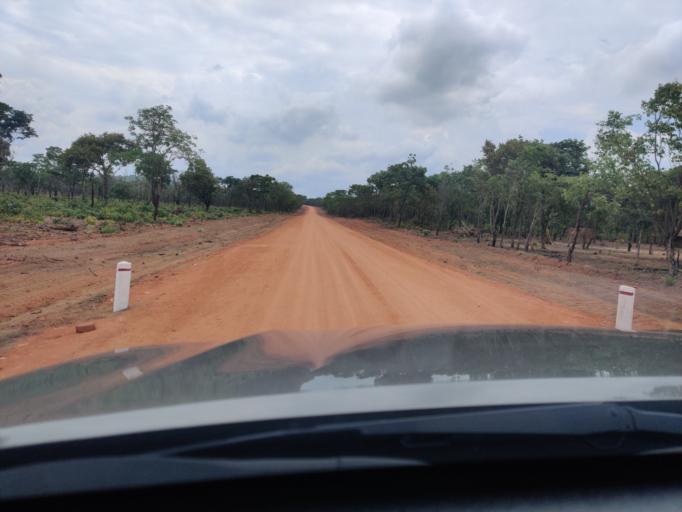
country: ZM
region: Central
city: Mkushi
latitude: -13.8208
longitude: 29.8694
